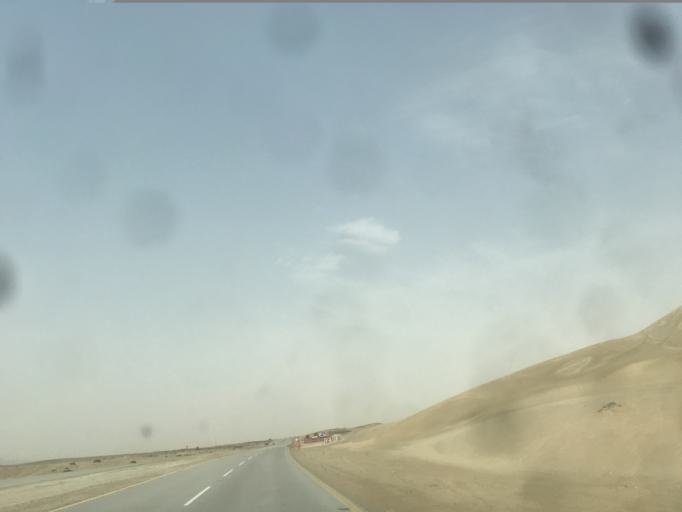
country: SA
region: Eastern Province
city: Abqaiq
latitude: 25.9084
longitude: 49.8881
